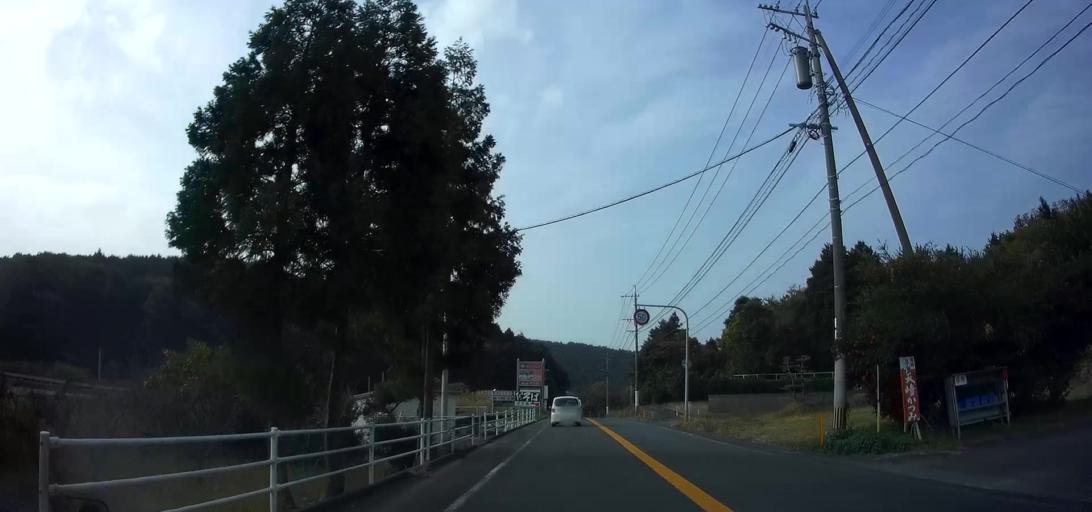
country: JP
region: Nagasaki
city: Shimabara
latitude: 32.7635
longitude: 130.2119
